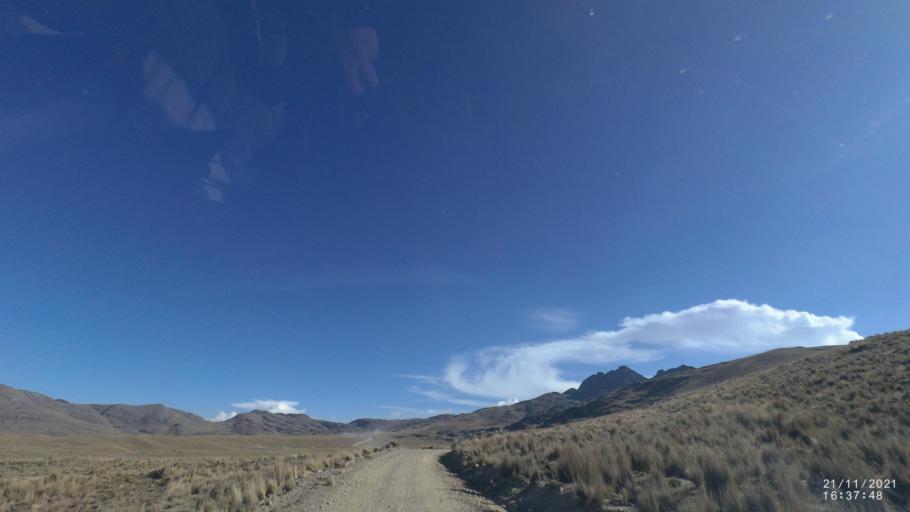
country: BO
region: Cochabamba
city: Cochabamba
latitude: -17.0473
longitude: -66.2633
